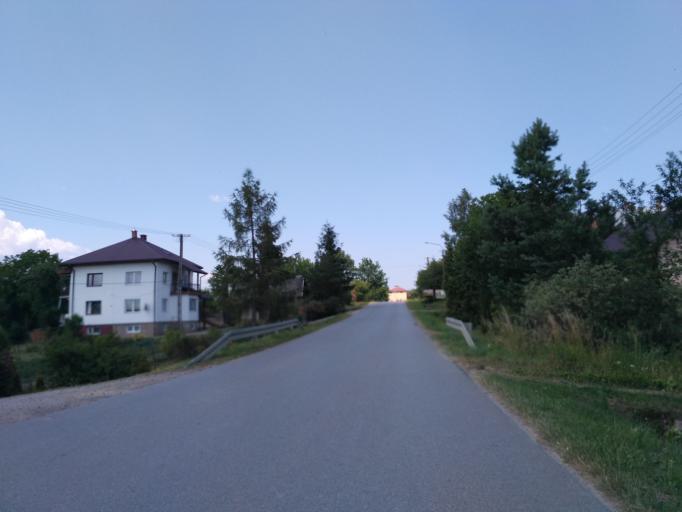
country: PL
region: Subcarpathian Voivodeship
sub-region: Powiat sanocki
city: Niebieszczany
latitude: 49.5151
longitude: 22.1402
